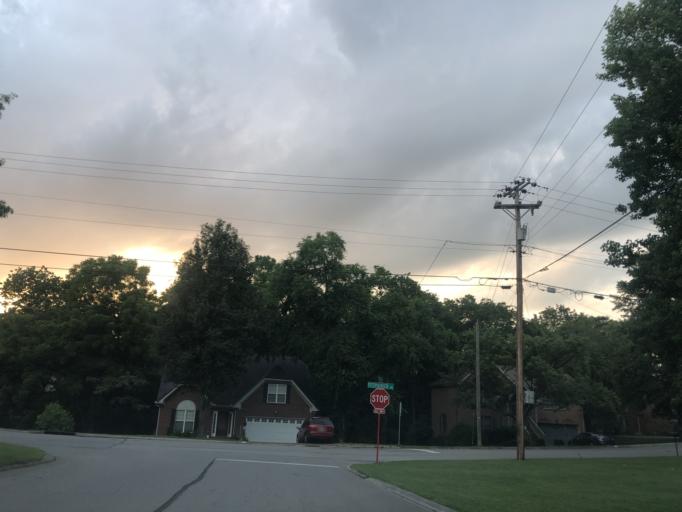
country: US
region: Tennessee
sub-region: Davidson County
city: Lakewood
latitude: 36.1447
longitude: -86.6324
